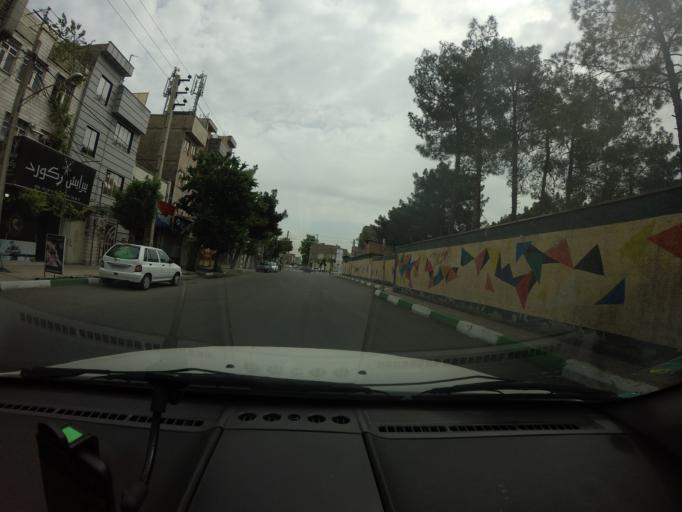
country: IR
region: Tehran
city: Eslamshahr
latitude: 35.5490
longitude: 51.2482
